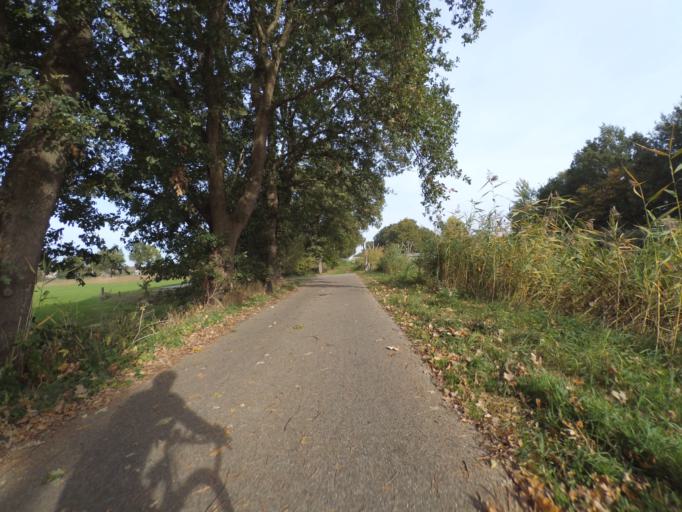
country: NL
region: Overijssel
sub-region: Gemeente Raalte
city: Raalte
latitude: 52.3689
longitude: 6.2767
